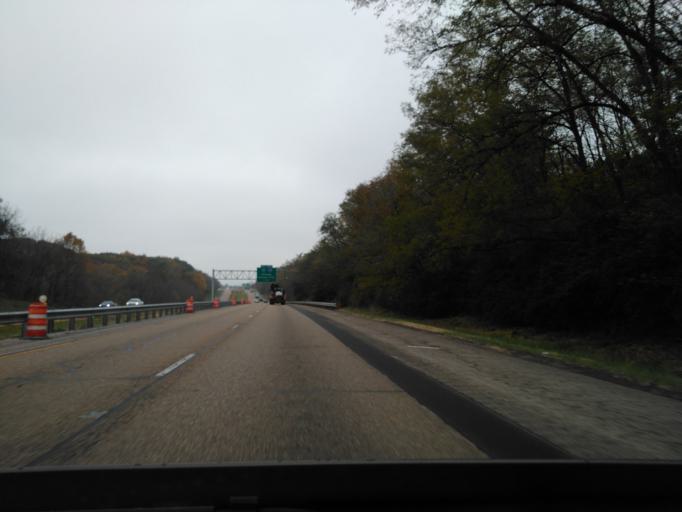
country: US
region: Illinois
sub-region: Madison County
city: Troy
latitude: 38.7556
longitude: -89.8776
